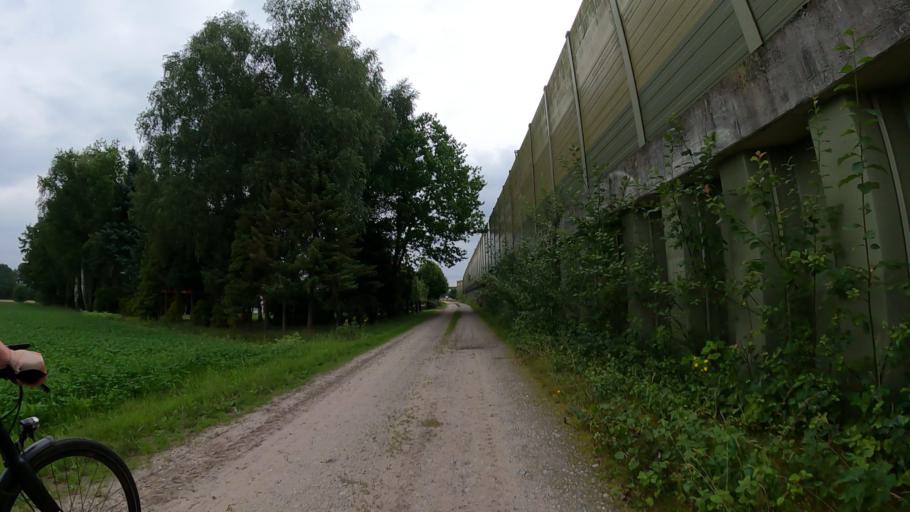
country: DE
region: Lower Saxony
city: Stelle
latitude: 53.3692
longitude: 10.1445
